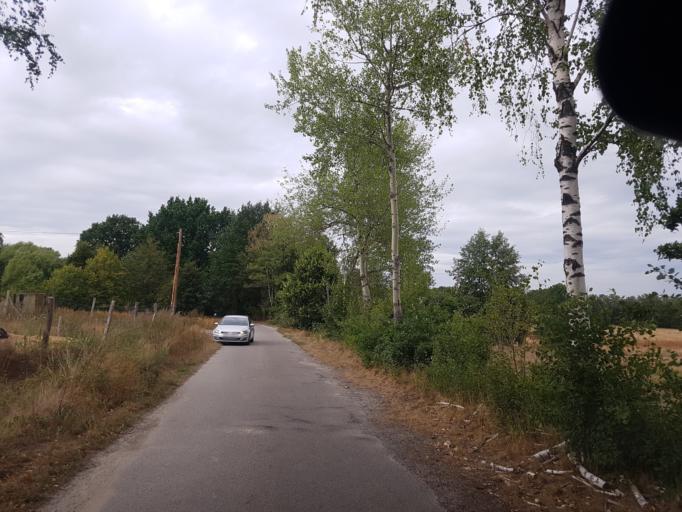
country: DE
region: Brandenburg
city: Calau
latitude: 51.7166
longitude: 13.9478
